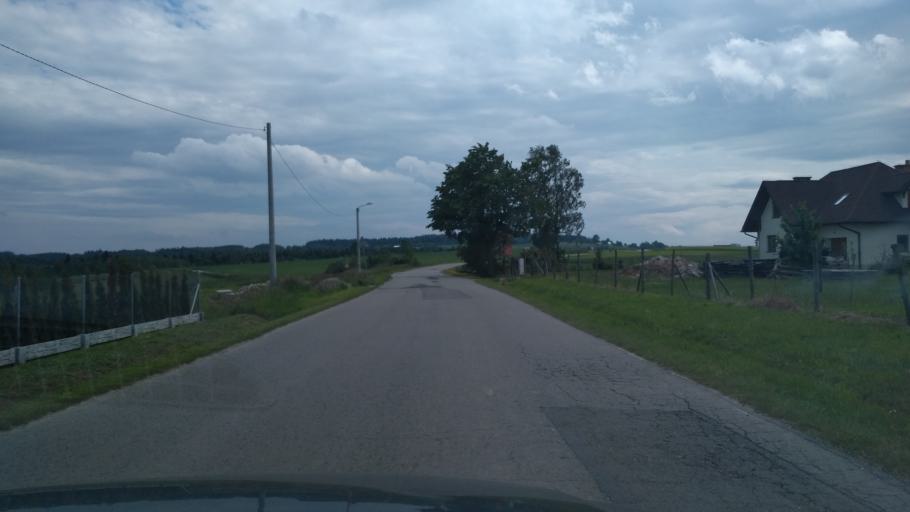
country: PL
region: Subcarpathian Voivodeship
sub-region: Powiat ropczycko-sedziszowski
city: Ropczyce
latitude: 50.0003
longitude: 21.6130
